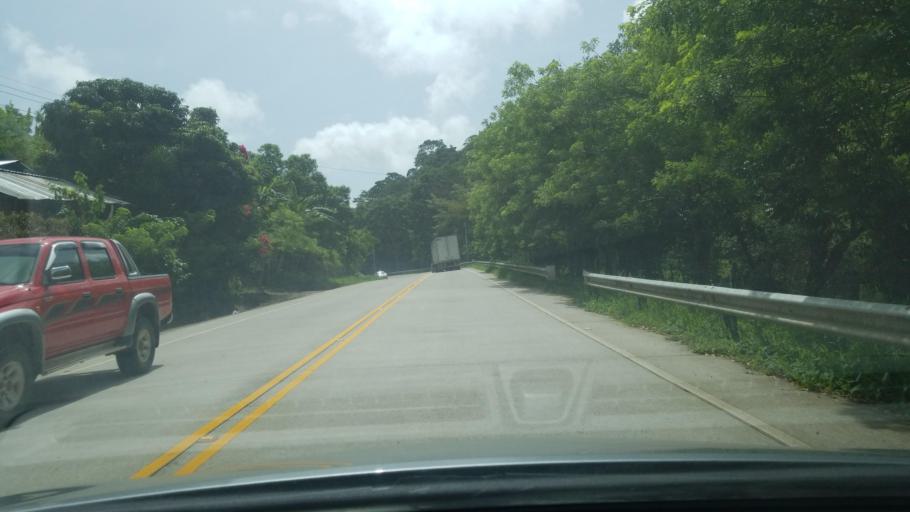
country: HN
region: Copan
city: San Jeronimo
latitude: 14.9469
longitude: -88.9119
